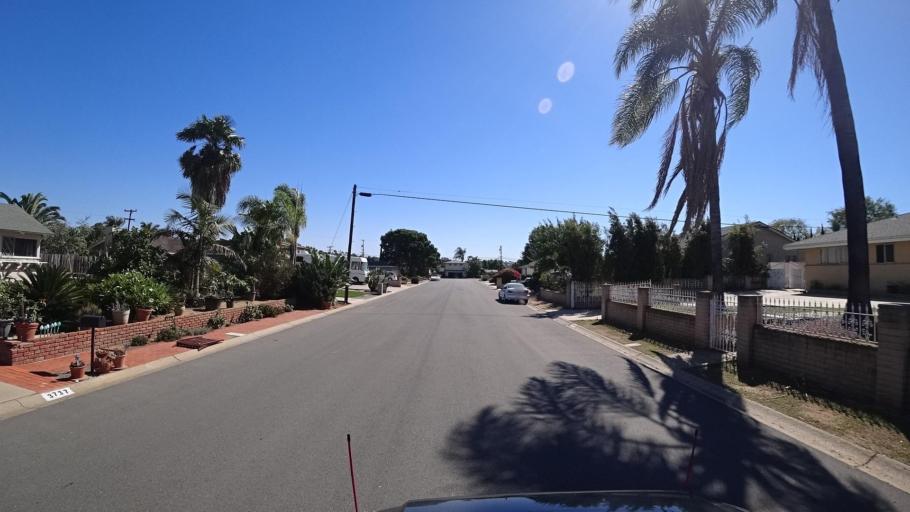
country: US
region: California
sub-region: San Diego County
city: Chula Vista
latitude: 32.6556
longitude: -117.0600
